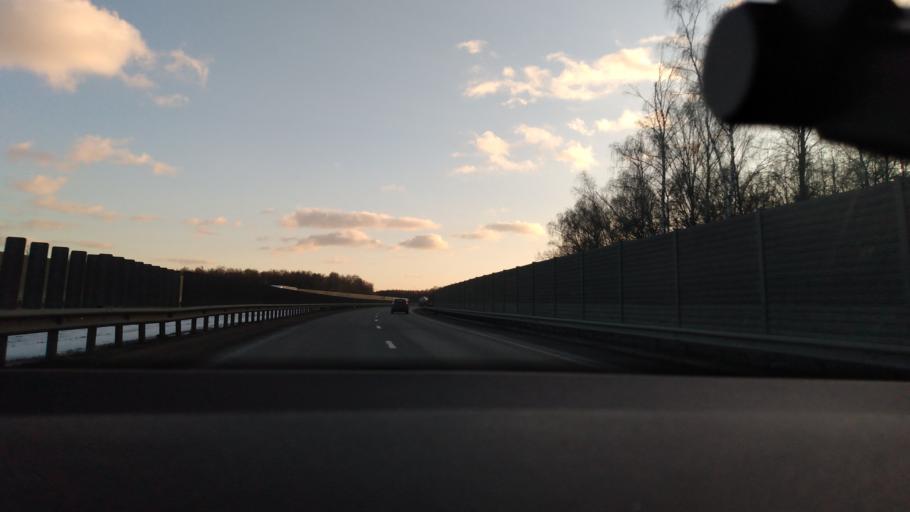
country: RU
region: Moskovskaya
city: Bronnitsy
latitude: 55.3980
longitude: 38.2454
